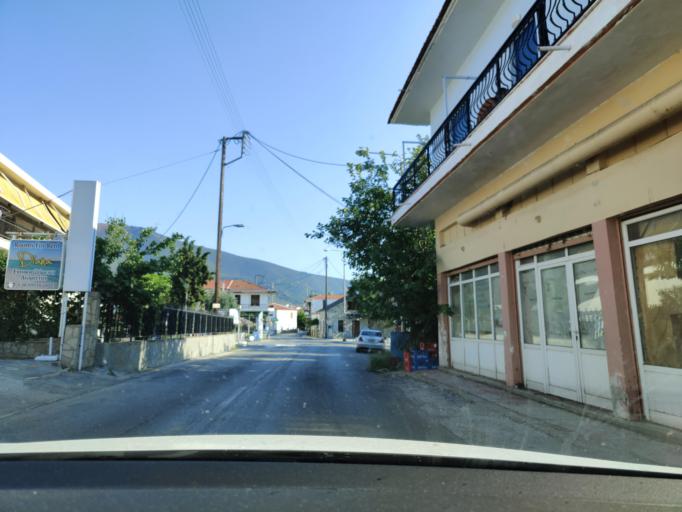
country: GR
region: East Macedonia and Thrace
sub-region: Nomos Kavalas
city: Prinos
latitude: 40.7089
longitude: 24.5342
